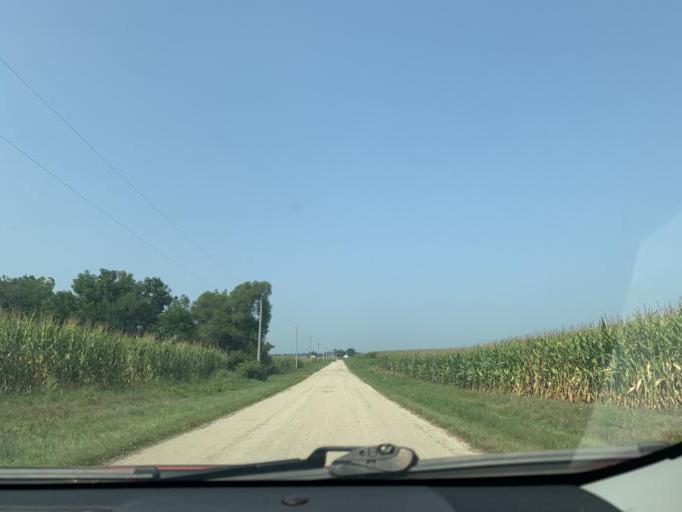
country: US
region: Illinois
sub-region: Whiteside County
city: Morrison
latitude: 41.8698
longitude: -89.8897
